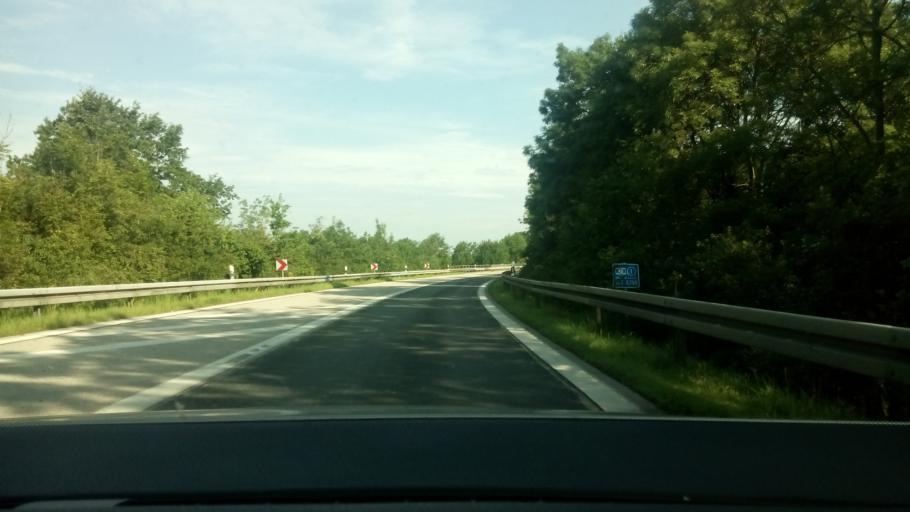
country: DE
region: Bavaria
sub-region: Upper Bavaria
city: Oberschleissheim
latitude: 48.2277
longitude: 11.5447
